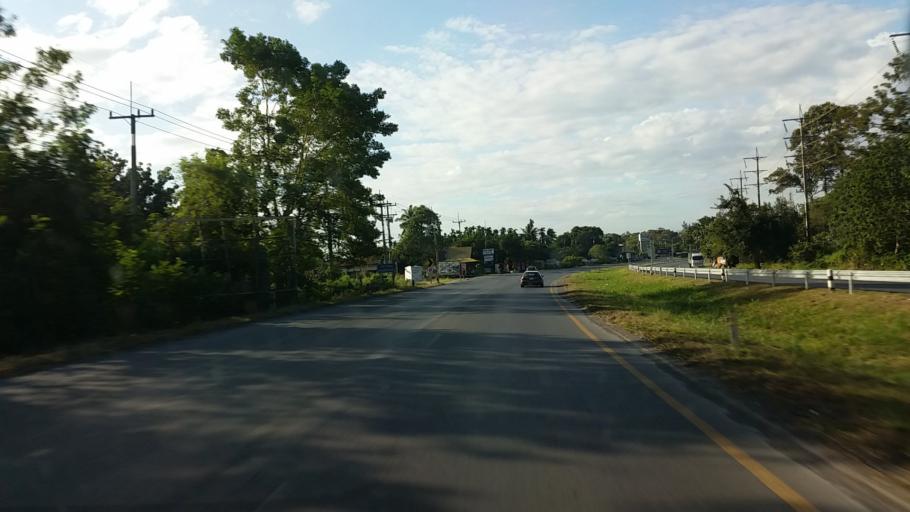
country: TH
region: Sara Buri
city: Chaloem Phra Kiat
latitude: 14.6713
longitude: 100.8935
